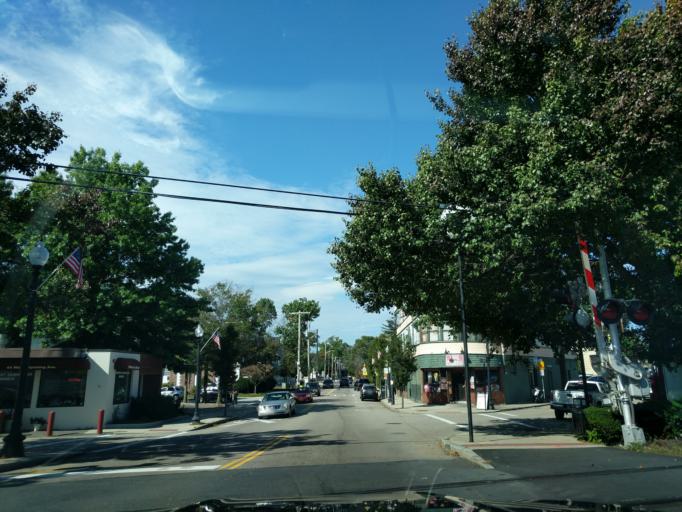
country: US
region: Massachusetts
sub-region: Middlesex County
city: Melrose
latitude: 42.4521
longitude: -71.0693
